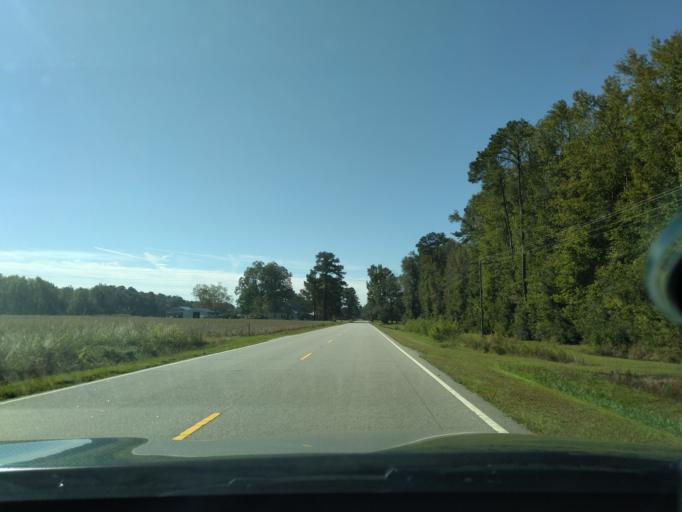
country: US
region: North Carolina
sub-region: Washington County
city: Plymouth
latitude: 35.7108
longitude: -76.7594
